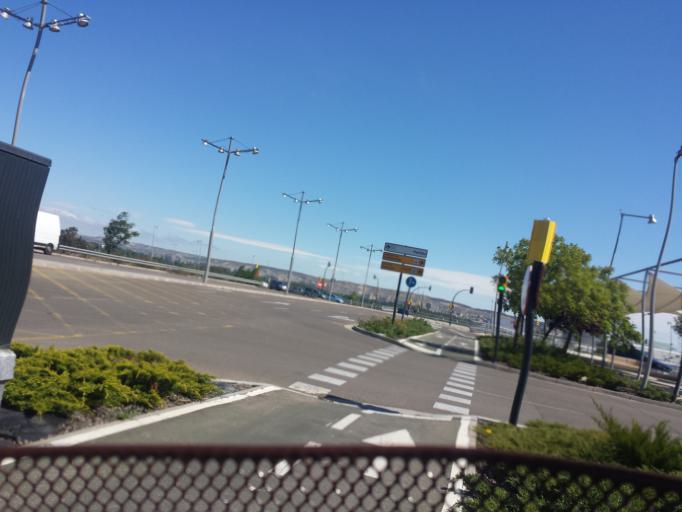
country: ES
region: Aragon
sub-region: Provincia de Zaragoza
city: Delicias
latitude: 41.6600
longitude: -0.9149
